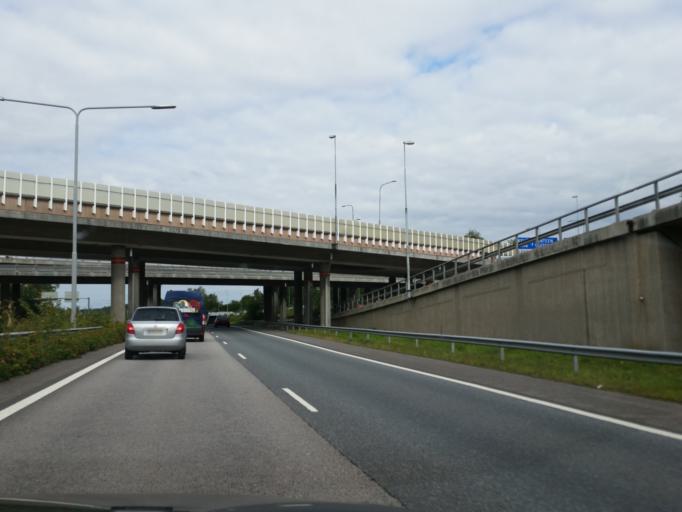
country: FI
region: Uusimaa
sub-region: Helsinki
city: Helsinki
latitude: 60.2435
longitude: 24.9480
